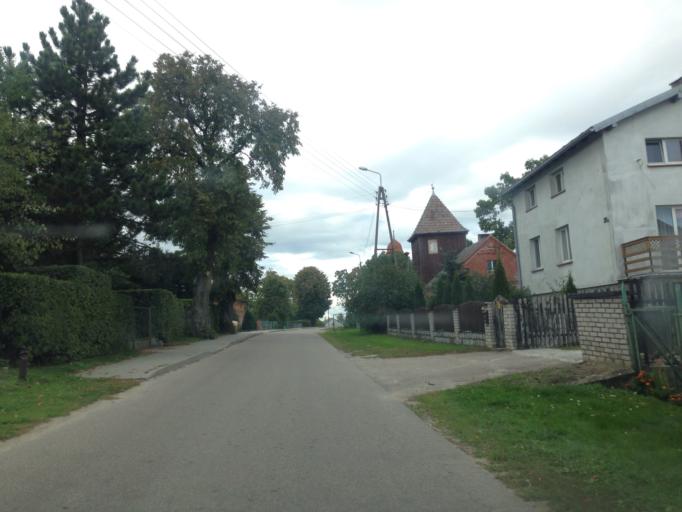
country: PL
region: Pomeranian Voivodeship
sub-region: Powiat kwidzynski
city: Prabuty
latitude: 53.7761
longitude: 19.2626
